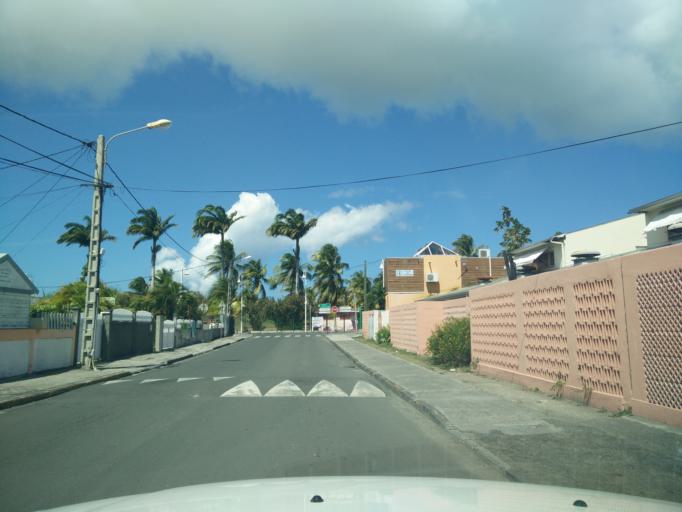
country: GP
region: Guadeloupe
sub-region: Guadeloupe
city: Saint-Francois
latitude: 16.2539
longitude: -61.2701
